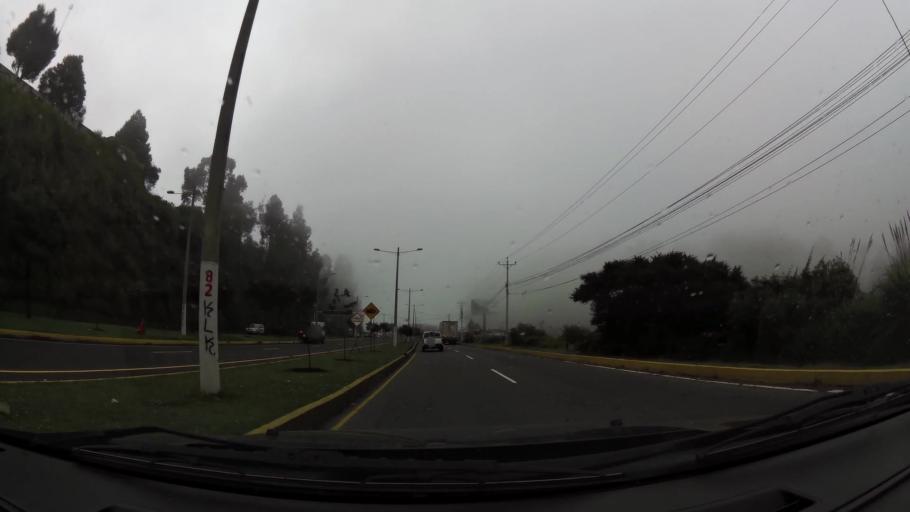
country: EC
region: Pichincha
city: Quito
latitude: -0.2471
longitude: -78.4844
